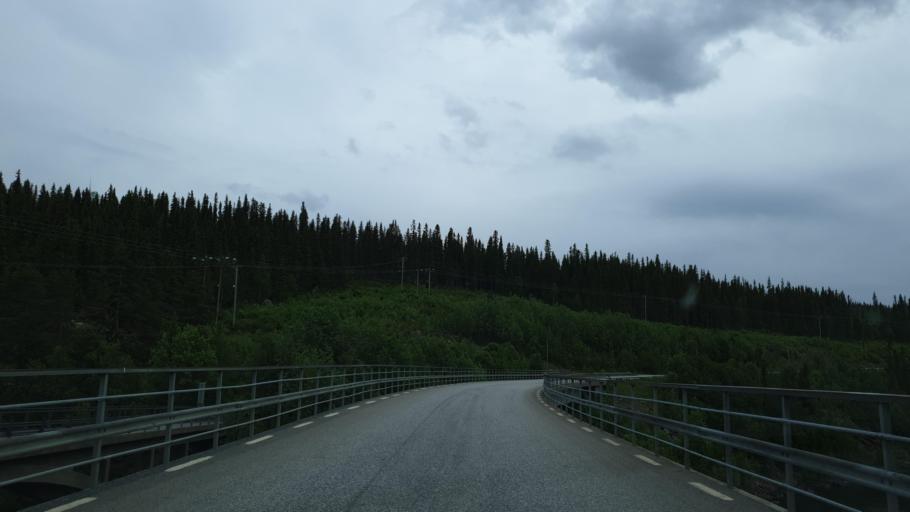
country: SE
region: Vaesterbotten
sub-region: Storumans Kommun
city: Fristad
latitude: 65.4243
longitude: 16.1715
